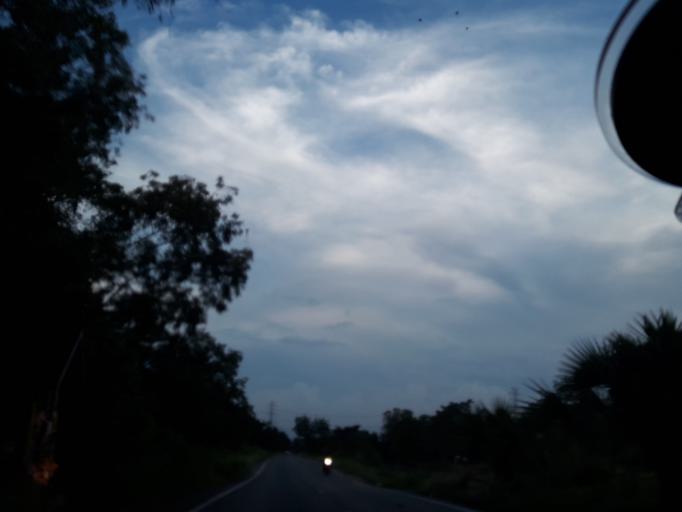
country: TH
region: Pathum Thani
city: Nong Suea
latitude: 14.1918
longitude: 100.8689
